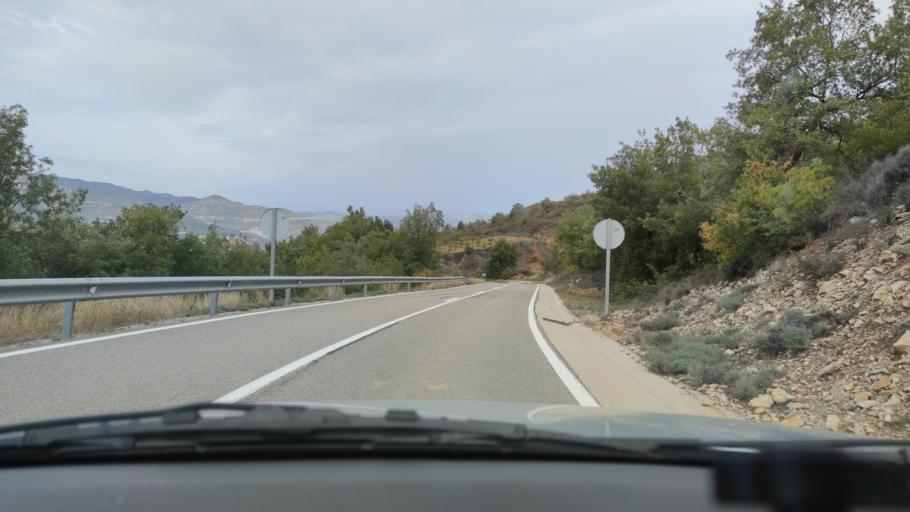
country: ES
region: Catalonia
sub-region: Provincia de Lleida
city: Llimiana
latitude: 42.0667
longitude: 0.9126
